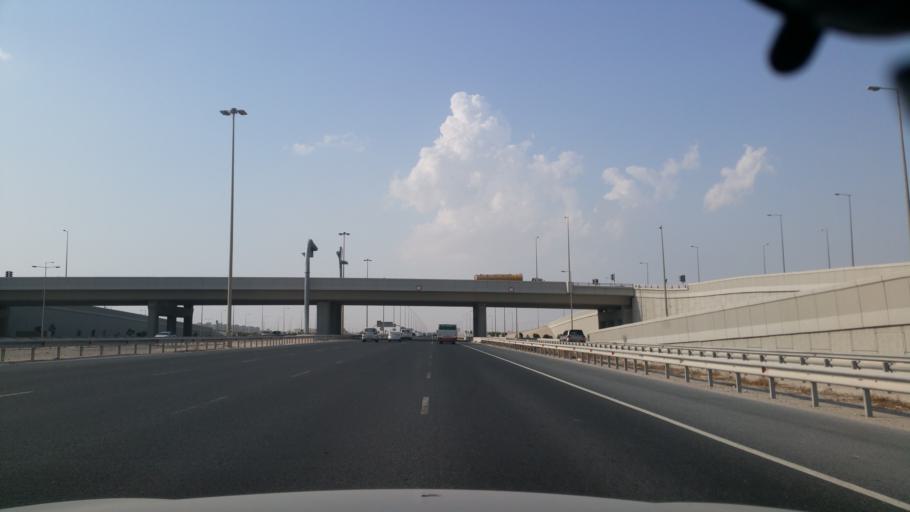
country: QA
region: Baladiyat Umm Salal
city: Umm Salal Muhammad
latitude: 25.4097
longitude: 51.4255
